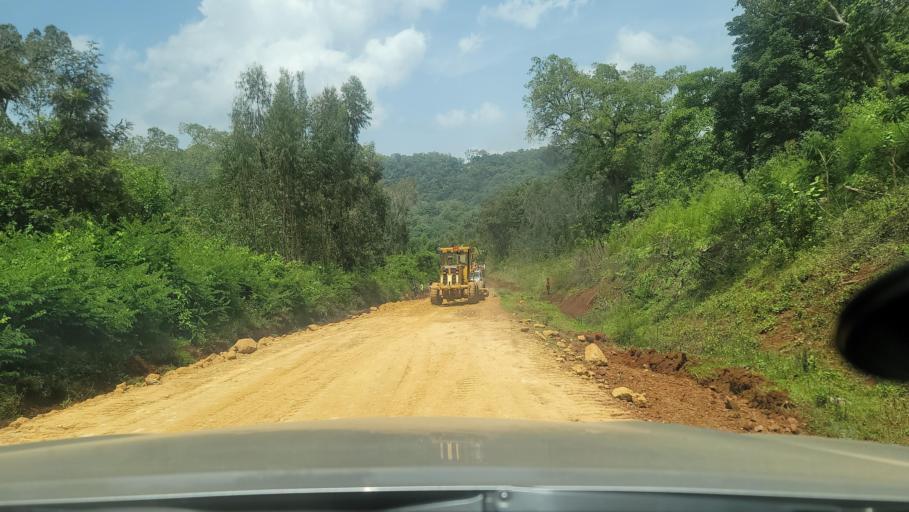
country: ET
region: Southern Nations, Nationalities, and People's Region
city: Bonga
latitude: 7.6946
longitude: 36.2449
